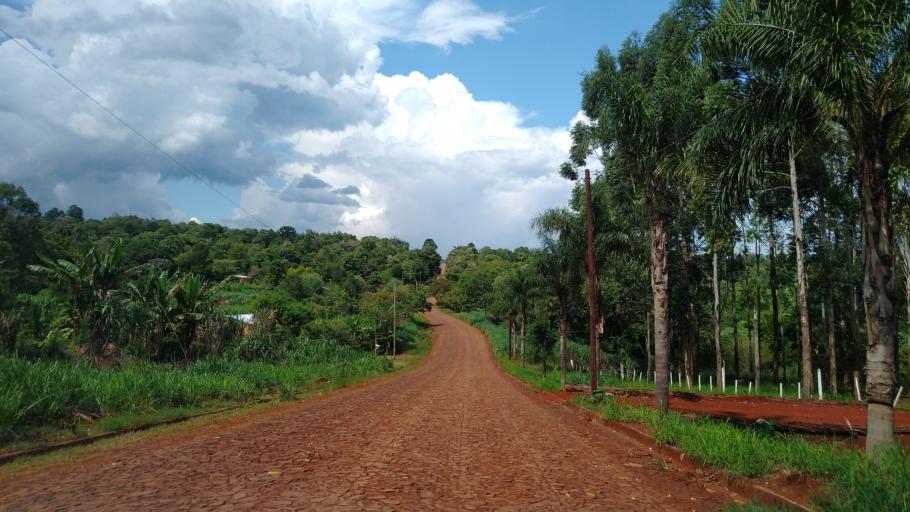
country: AR
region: Misiones
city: Puerto Libertad
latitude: -25.9656
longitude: -54.6026
